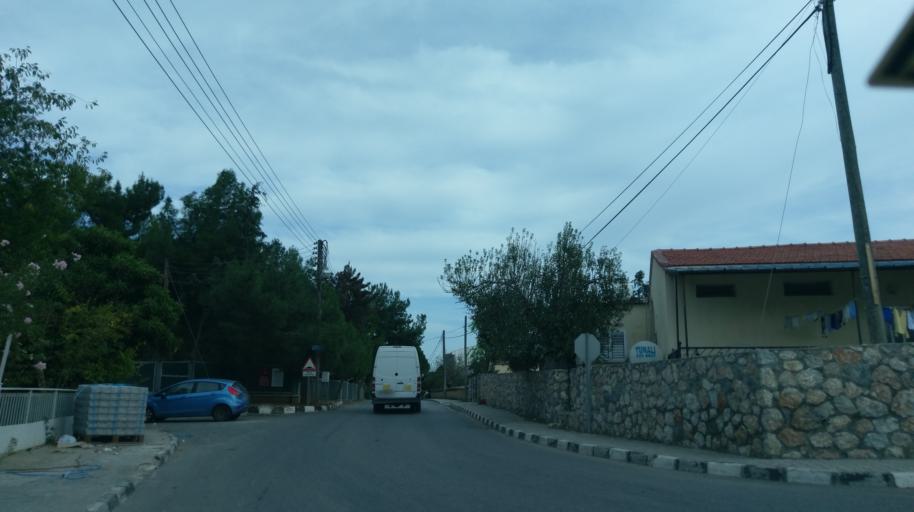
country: CY
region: Keryneia
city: Kyrenia
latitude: 35.2661
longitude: 33.3263
